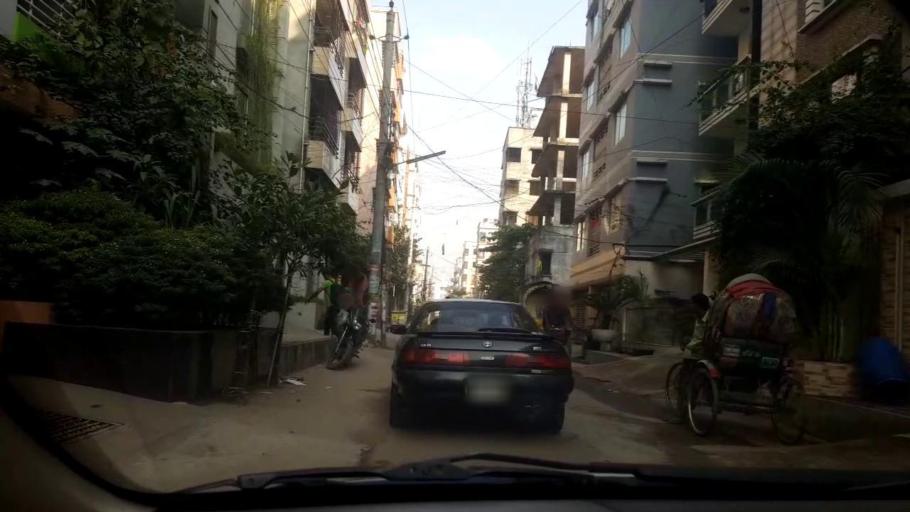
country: BD
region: Dhaka
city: Tungi
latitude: 23.8699
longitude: 90.3796
